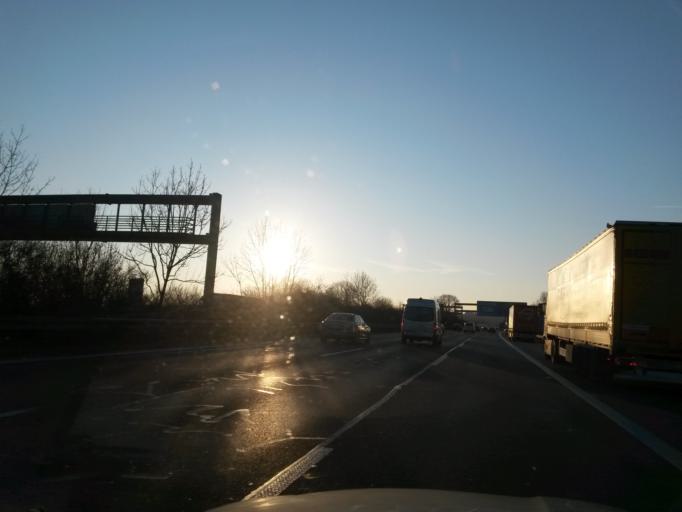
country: DE
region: Bavaria
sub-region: Upper Bavaria
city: Aschheim
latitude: 48.1864
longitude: 11.7157
